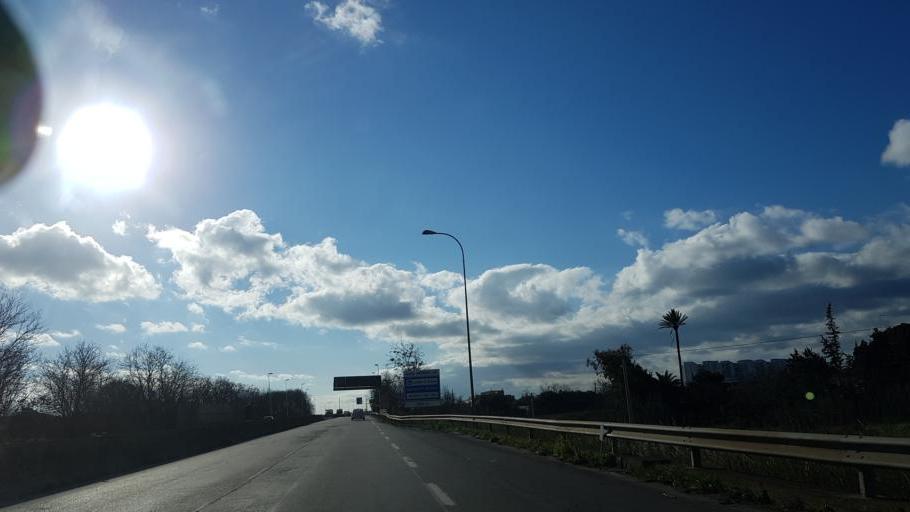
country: IT
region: Apulia
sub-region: Provincia di Brindisi
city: Brindisi
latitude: 40.6321
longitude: 17.9175
